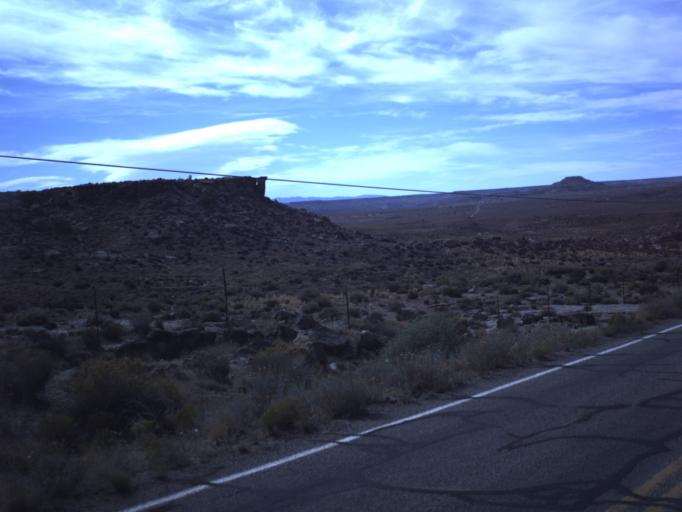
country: US
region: Utah
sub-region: San Juan County
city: Blanding
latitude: 37.2742
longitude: -109.2984
